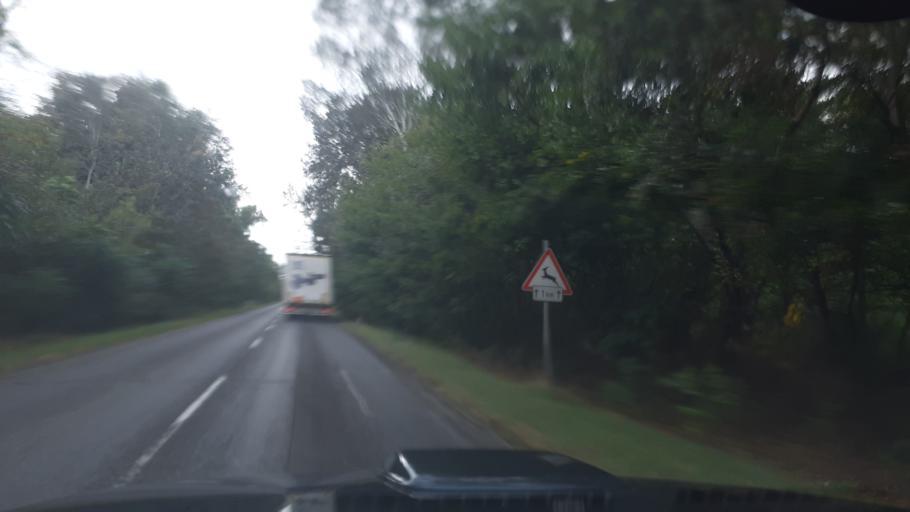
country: HU
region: Bacs-Kiskun
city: Balloszog
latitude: 46.8880
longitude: 19.5631
